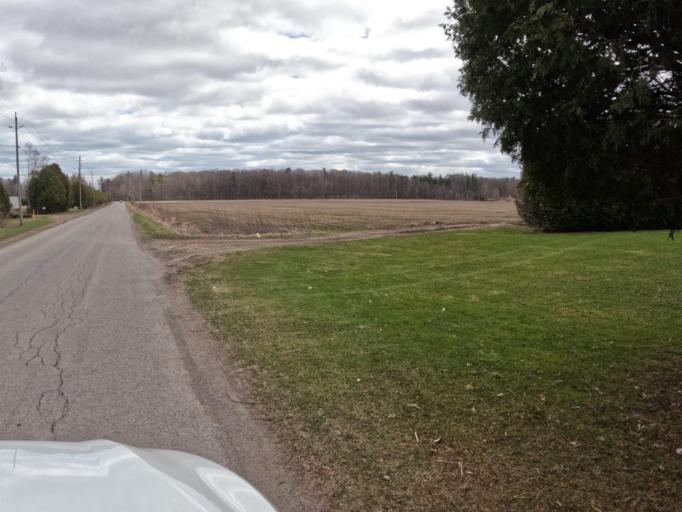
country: CA
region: Ontario
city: Norfolk County
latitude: 42.7953
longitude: -80.3613
